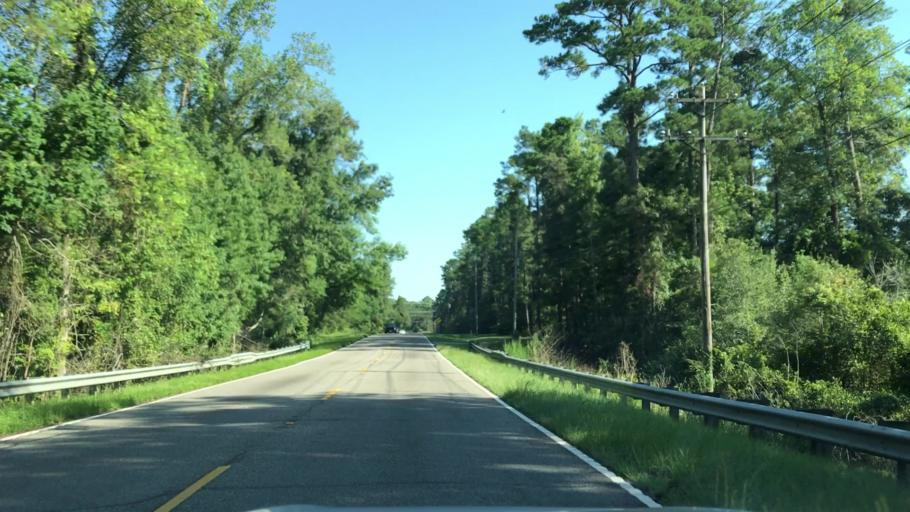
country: US
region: South Carolina
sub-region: Georgetown County
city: Georgetown
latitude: 33.4540
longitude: -79.2802
